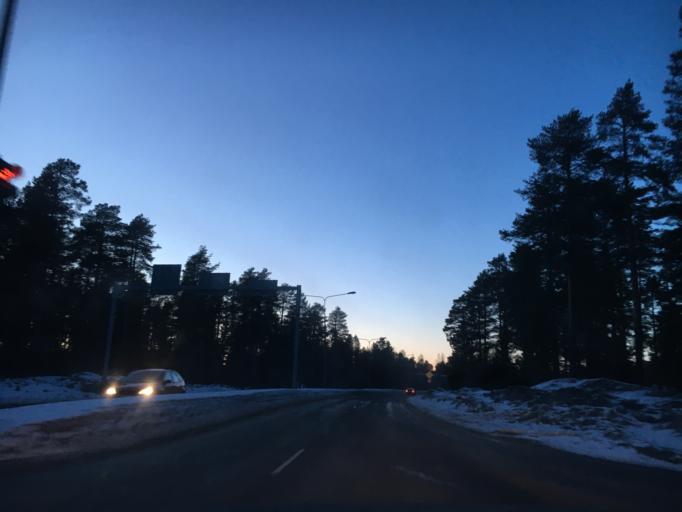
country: FI
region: Kainuu
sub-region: Kajaani
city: Kajaani
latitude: 64.2059
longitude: 27.7341
